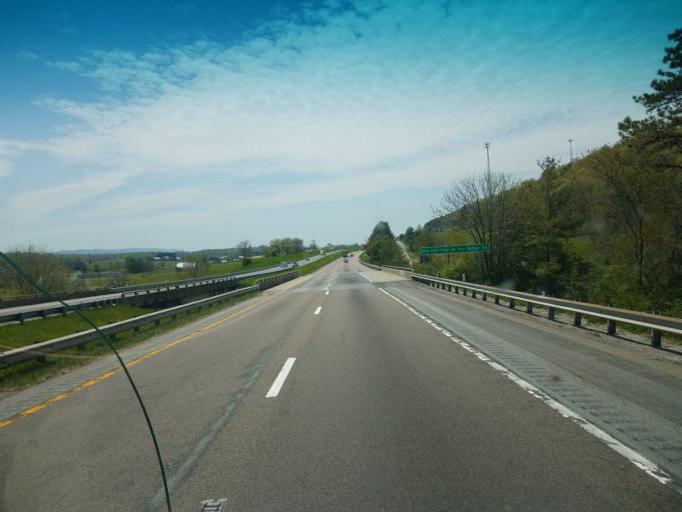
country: US
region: Virginia
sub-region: Wythe County
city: Rural Retreat
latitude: 36.9225
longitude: -81.2249
